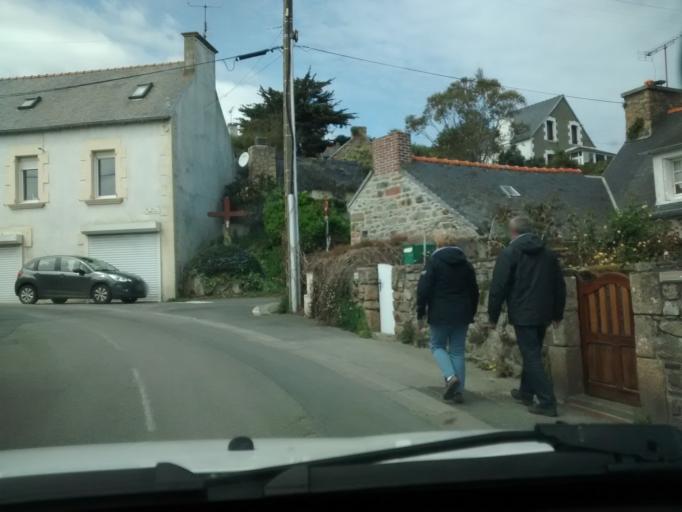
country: FR
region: Brittany
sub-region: Departement des Cotes-d'Armor
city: Ploubazlanec
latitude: 48.7998
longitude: -3.0059
